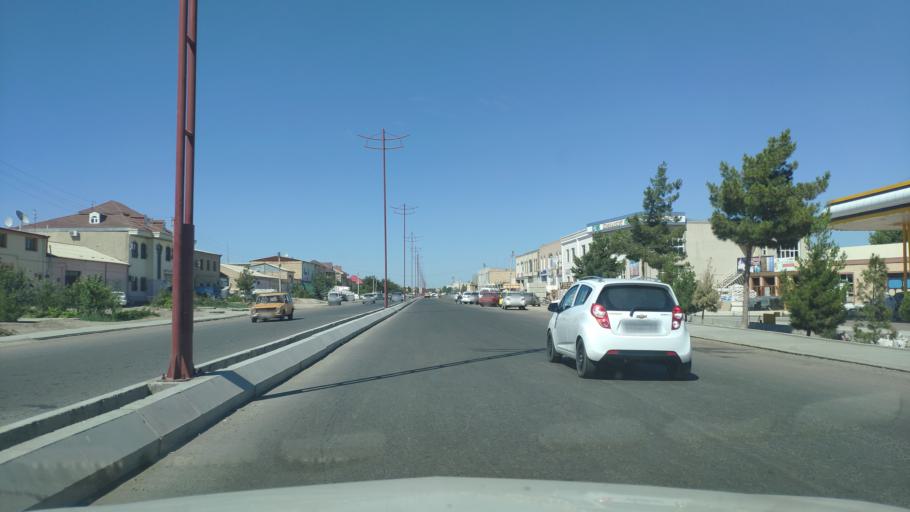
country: UZ
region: Bukhara
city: Bukhara
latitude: 39.7732
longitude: 64.3867
